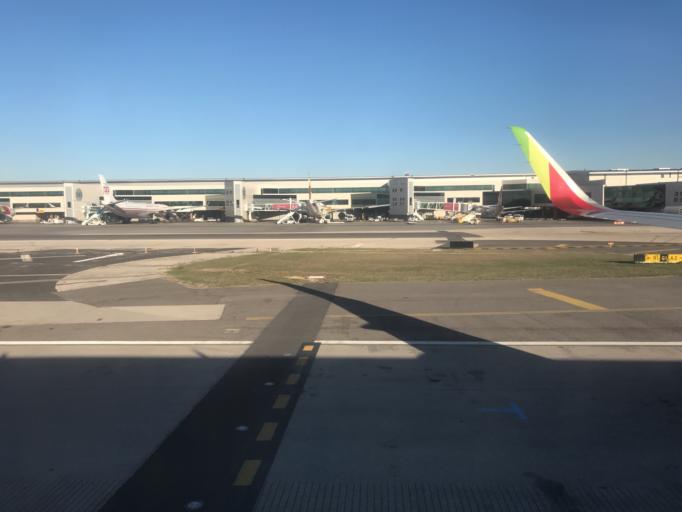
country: PT
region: Lisbon
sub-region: Loures
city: Camarate
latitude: 38.7737
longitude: -9.1337
